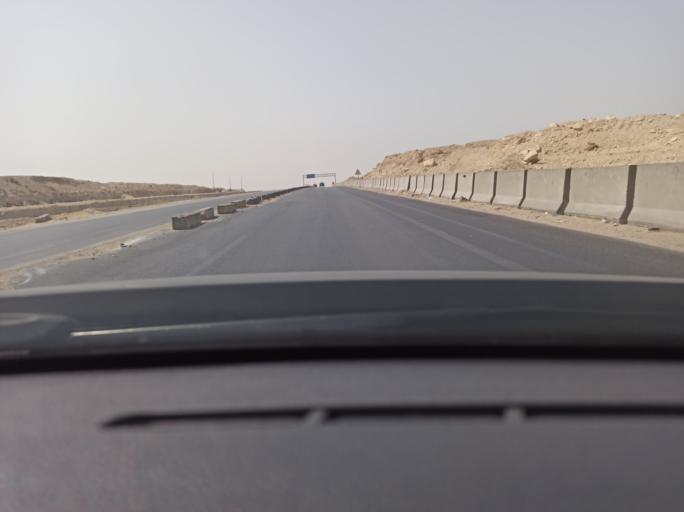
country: EG
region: Muhafazat al Fayyum
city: Al Wasitah
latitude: 29.2939
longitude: 31.2754
